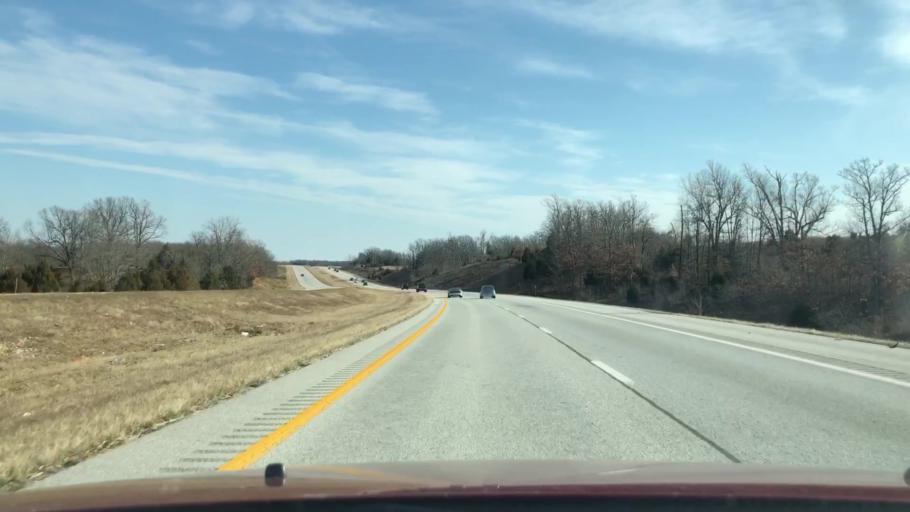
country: US
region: Missouri
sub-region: Webster County
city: Seymour
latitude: 37.1607
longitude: -92.8958
